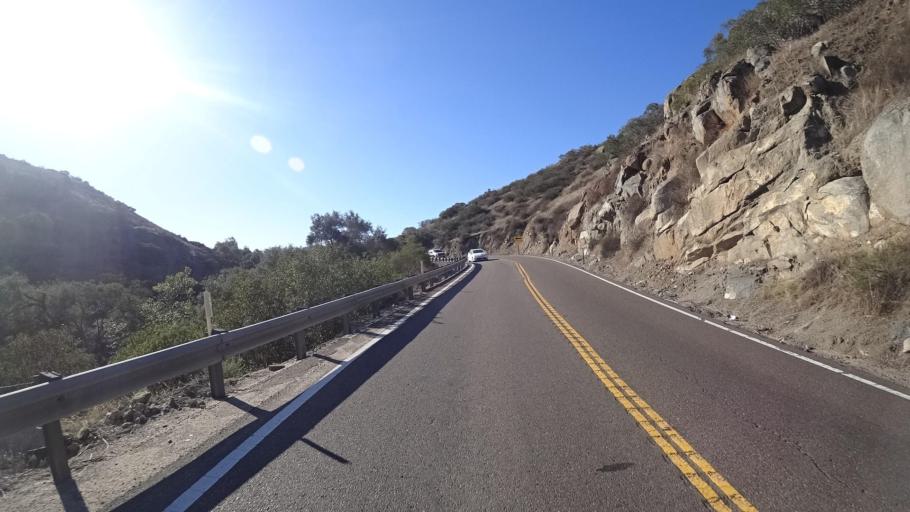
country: US
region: California
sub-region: San Diego County
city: Jamul
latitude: 32.6490
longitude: -116.7865
